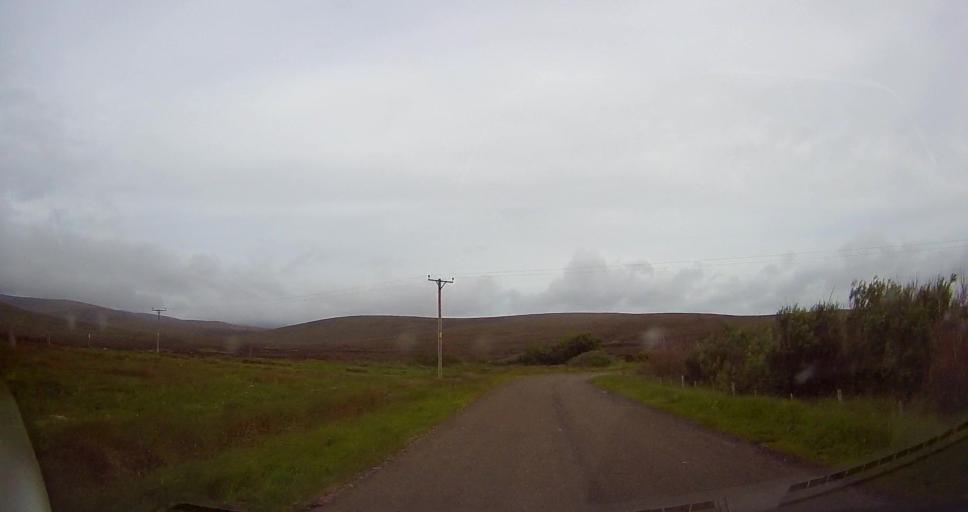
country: GB
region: Scotland
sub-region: Orkney Islands
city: Stromness
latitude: 58.8388
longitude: -3.2165
